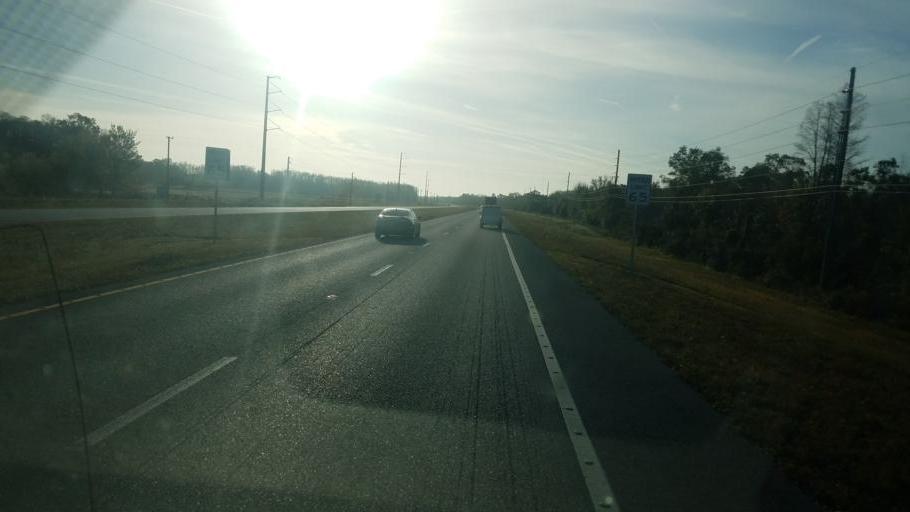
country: US
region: Florida
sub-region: Osceola County
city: Saint Cloud
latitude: 28.1555
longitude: -81.1097
